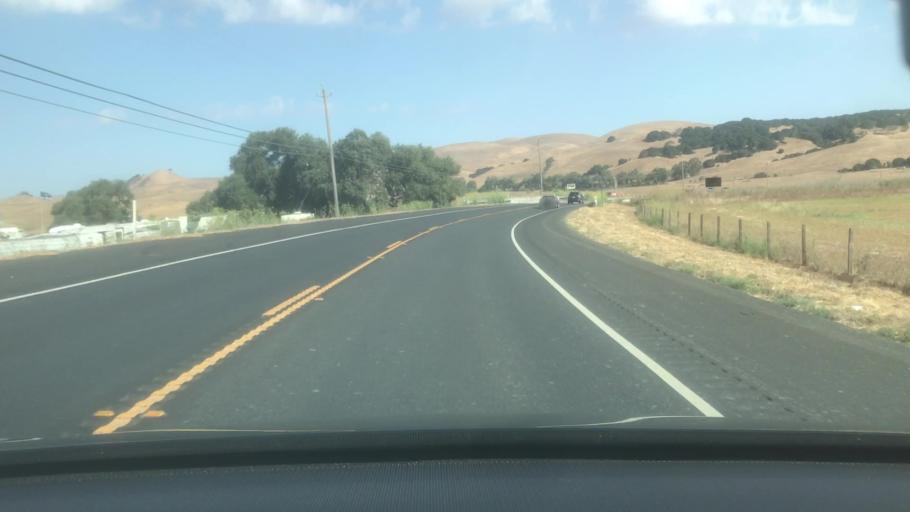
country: US
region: California
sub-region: Marin County
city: Black Point-Green Point
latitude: 38.1689
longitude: -122.4574
